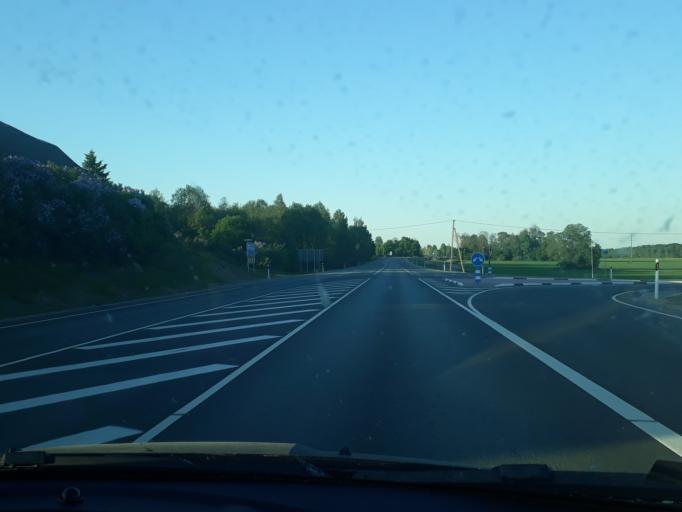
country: EE
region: Paernumaa
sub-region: Tootsi vald
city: Tootsi
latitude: 58.5047
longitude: 24.7948
